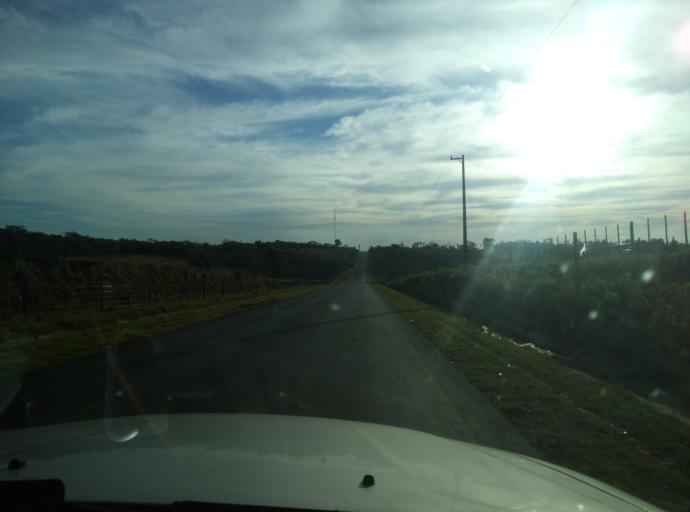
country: PY
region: Caaguazu
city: Carayao
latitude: -25.1544
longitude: -56.3168
